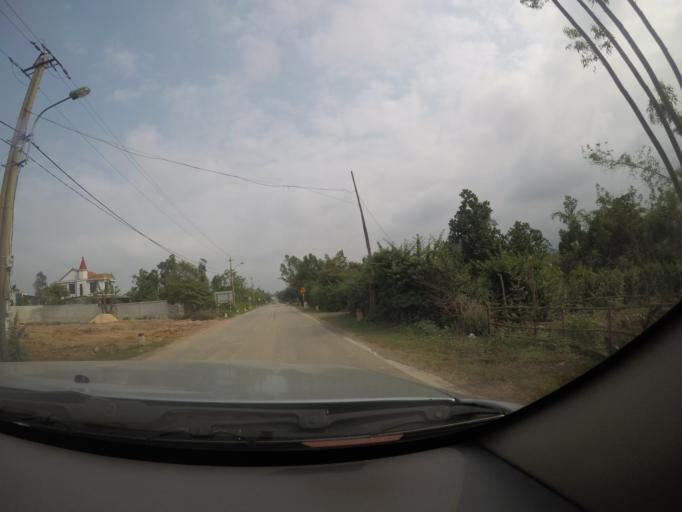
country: VN
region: Quang Binh
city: Kwang Binh
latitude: 17.4493
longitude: 106.5716
